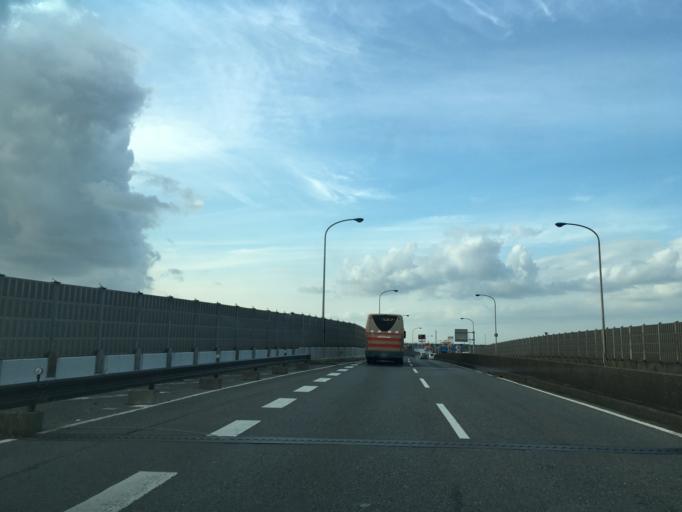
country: JP
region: Chiba
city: Kisarazu
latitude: 35.3903
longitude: 139.9409
